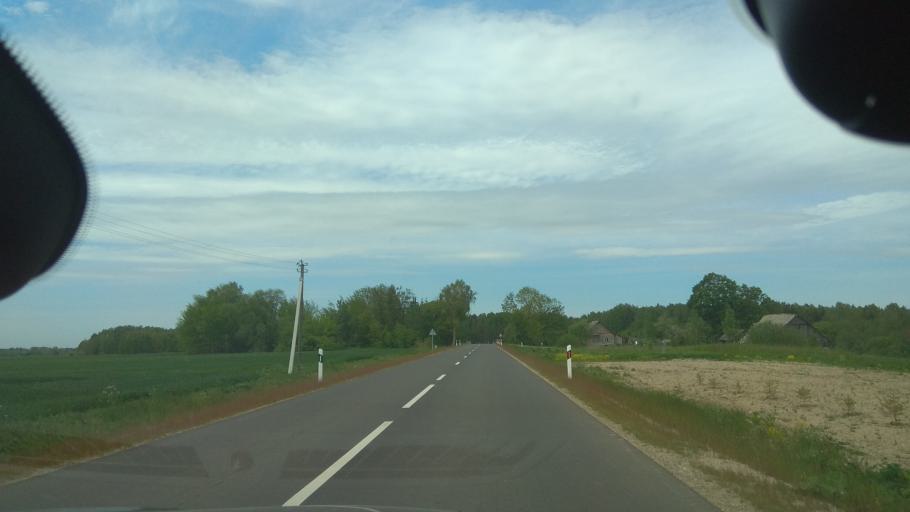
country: LT
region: Vilnius County
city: Ukmerge
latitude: 55.1178
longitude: 24.6300
